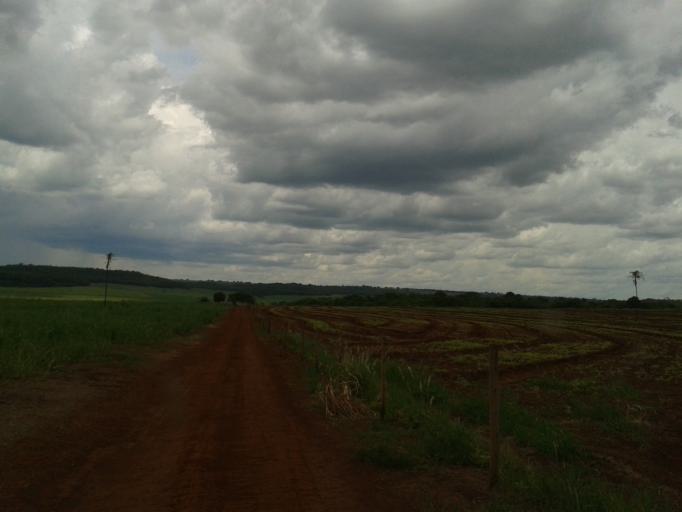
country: BR
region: Minas Gerais
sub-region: Centralina
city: Centralina
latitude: -18.6804
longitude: -49.2303
